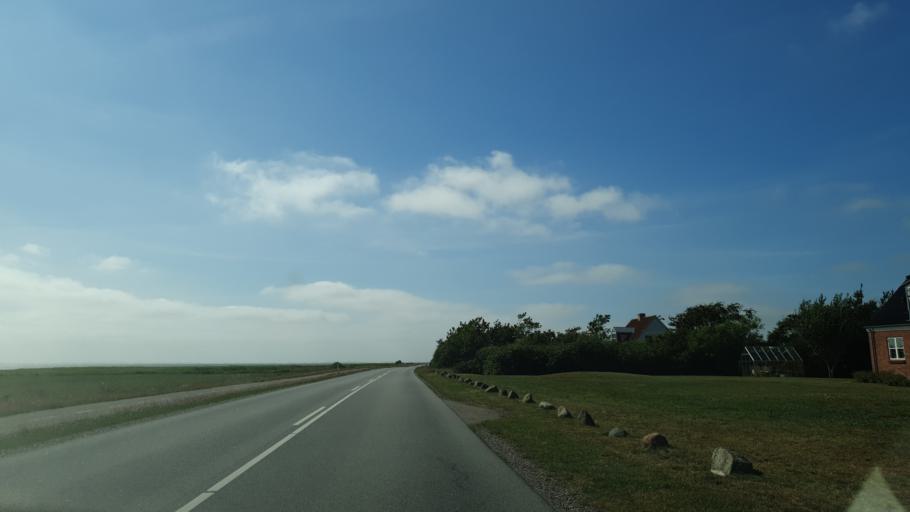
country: DK
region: Central Jutland
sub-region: Ringkobing-Skjern Kommune
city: Ringkobing
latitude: 56.0620
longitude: 8.2989
